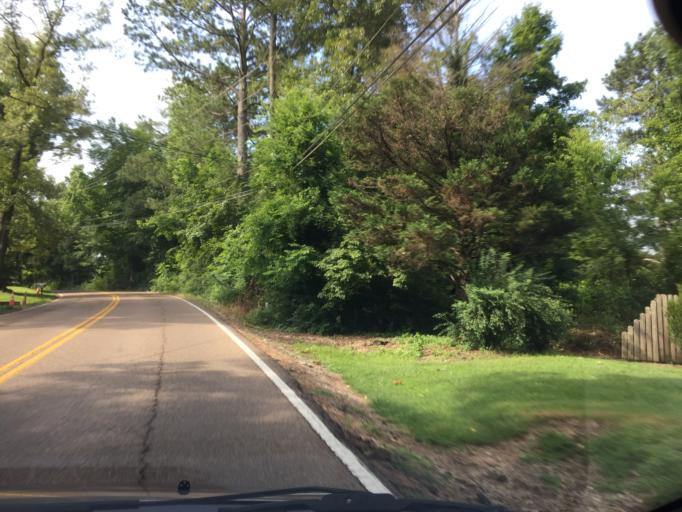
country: US
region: Tennessee
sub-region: Hamilton County
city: Apison
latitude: 35.0276
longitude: -85.0257
